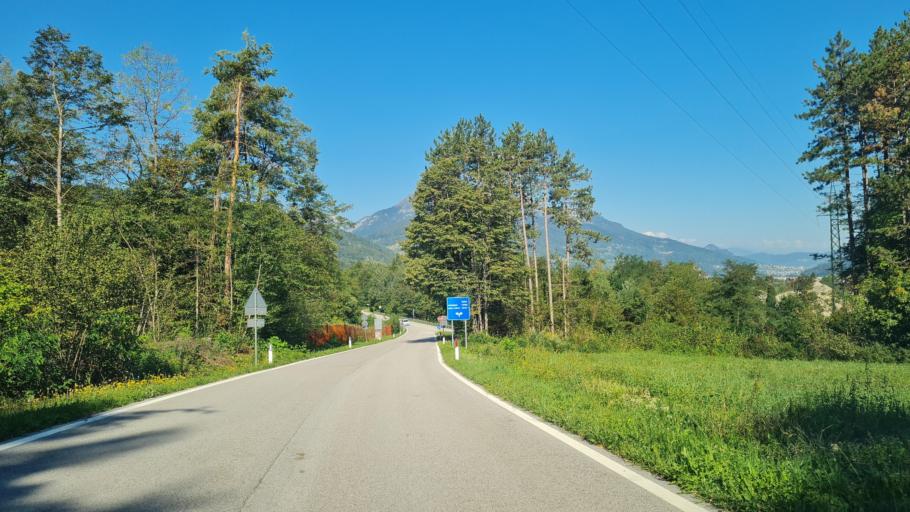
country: IT
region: Trentino-Alto Adige
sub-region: Provincia di Trento
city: Caldonazzo
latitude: 45.9844
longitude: 11.2806
